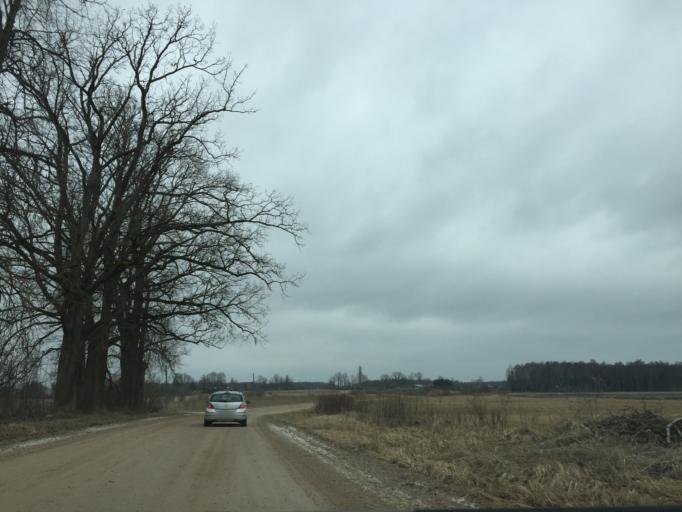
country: LV
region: Kegums
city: Kegums
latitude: 56.7668
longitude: 24.7724
